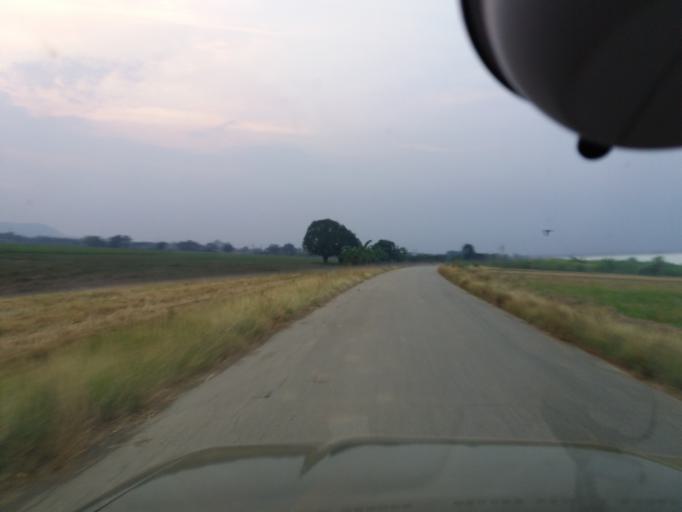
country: TH
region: Suphan Buri
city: Doem Bang Nang Buat
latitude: 14.8872
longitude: 100.1367
